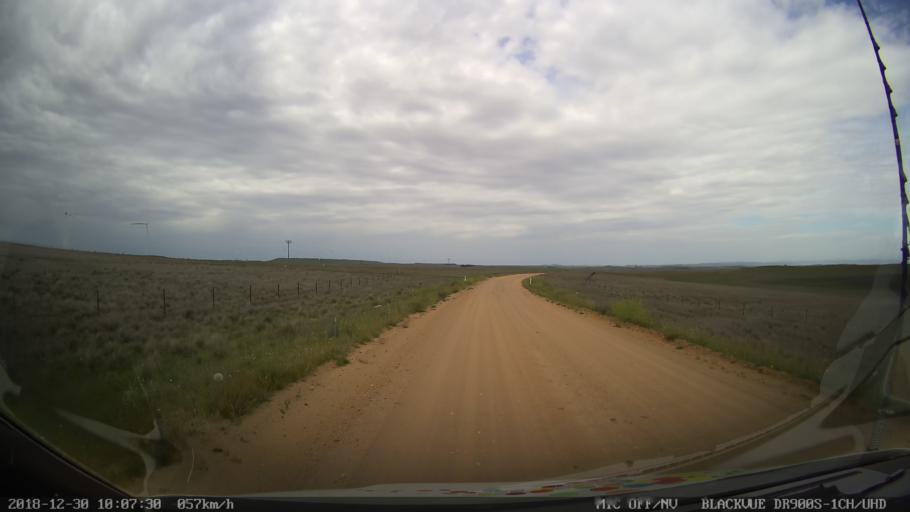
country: AU
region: New South Wales
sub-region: Cooma-Monaro
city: Cooma
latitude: -36.5399
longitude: 149.1222
